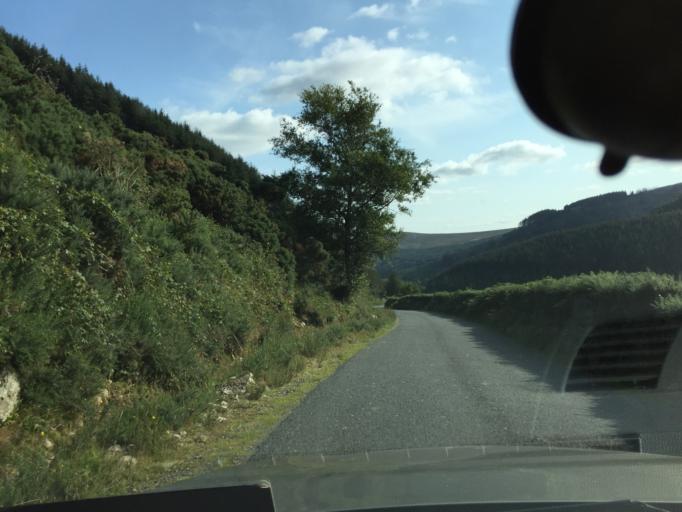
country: IE
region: Leinster
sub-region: Wicklow
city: Rathdrum
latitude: 53.0614
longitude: -6.3323
